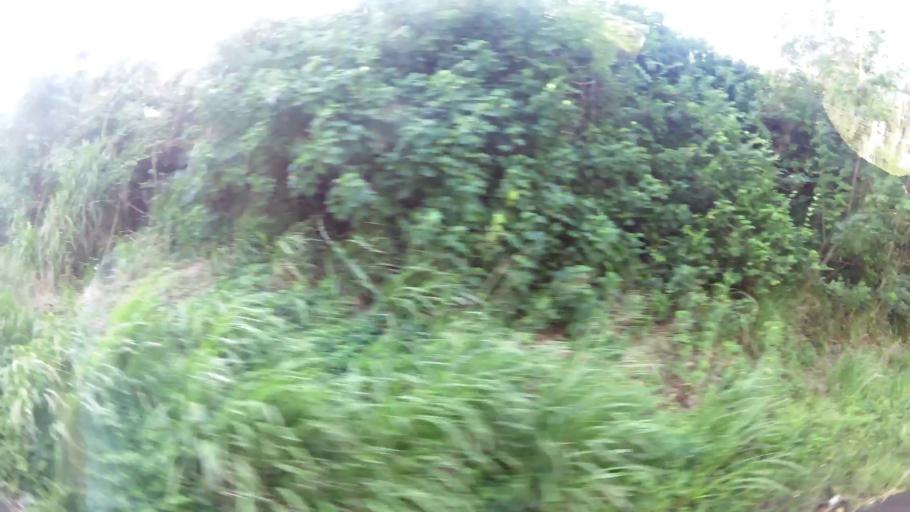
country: MQ
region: Martinique
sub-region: Martinique
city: Le Francois
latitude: 14.6199
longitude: -60.8924
